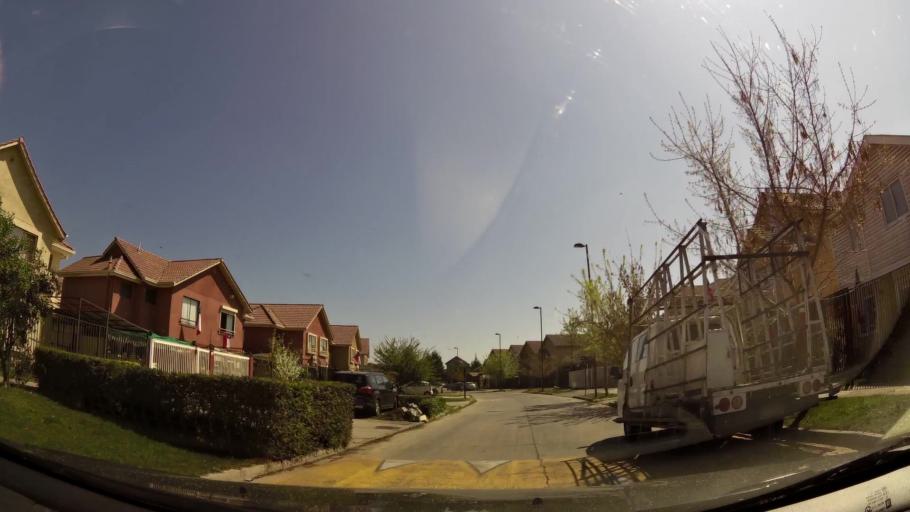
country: CL
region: Santiago Metropolitan
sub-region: Provincia de Chacabuco
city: Chicureo Abajo
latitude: -33.3234
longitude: -70.7504
